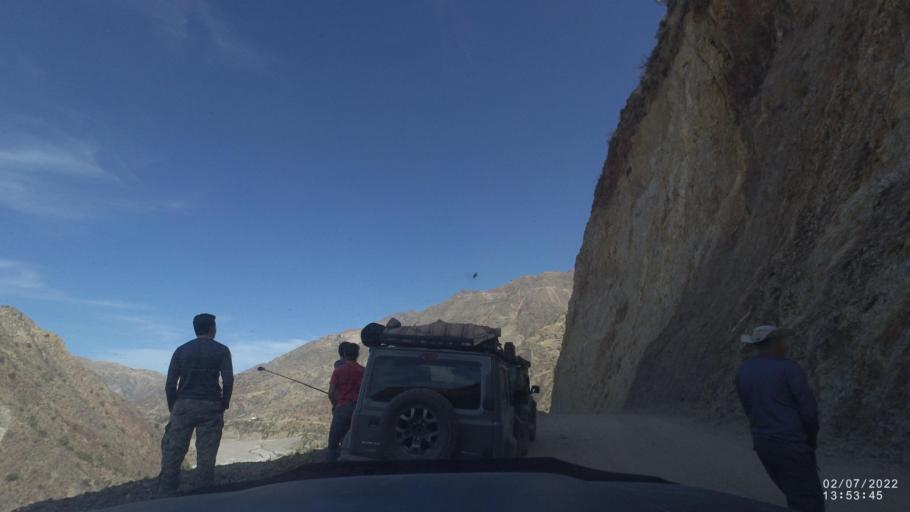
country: BO
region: Cochabamba
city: Irpa Irpa
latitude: -17.8250
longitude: -66.3833
